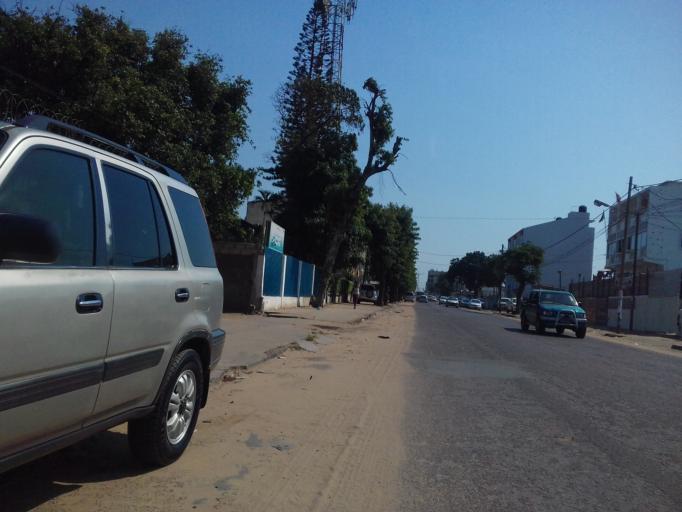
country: MZ
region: Maputo City
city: Maputo
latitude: -25.9503
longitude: 32.5695
